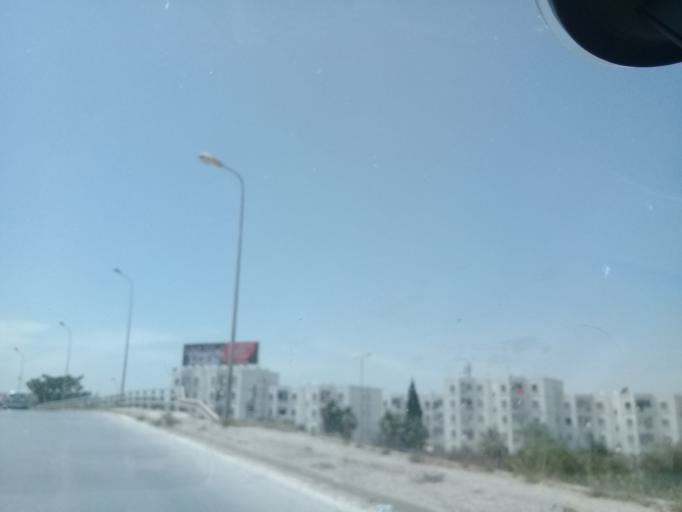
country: TN
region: Ariana
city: Ariana
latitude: 36.8271
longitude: 10.2012
